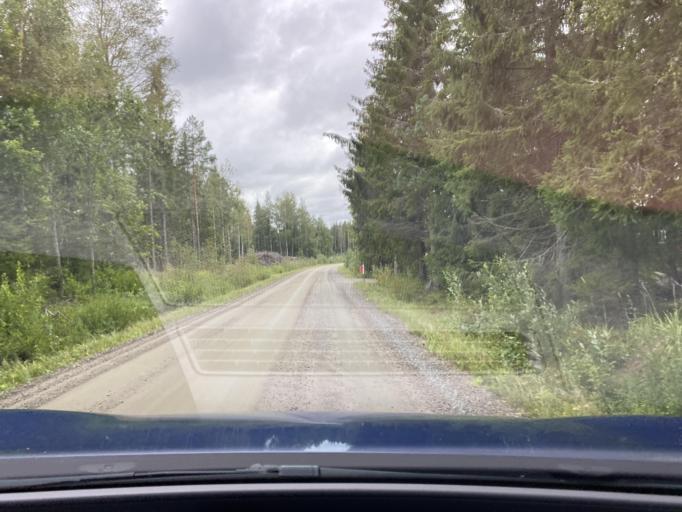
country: FI
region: Pirkanmaa
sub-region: Lounais-Pirkanmaa
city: Punkalaidun
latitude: 61.2060
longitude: 23.1782
